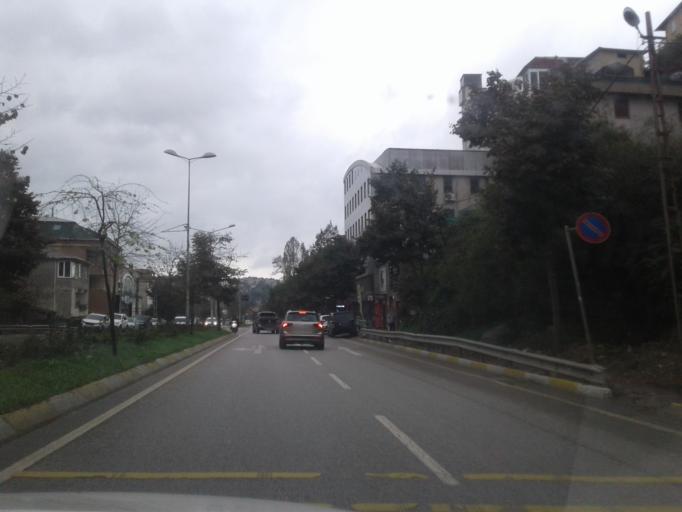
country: TR
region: Istanbul
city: Umraniye
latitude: 41.0827
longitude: 29.0828
